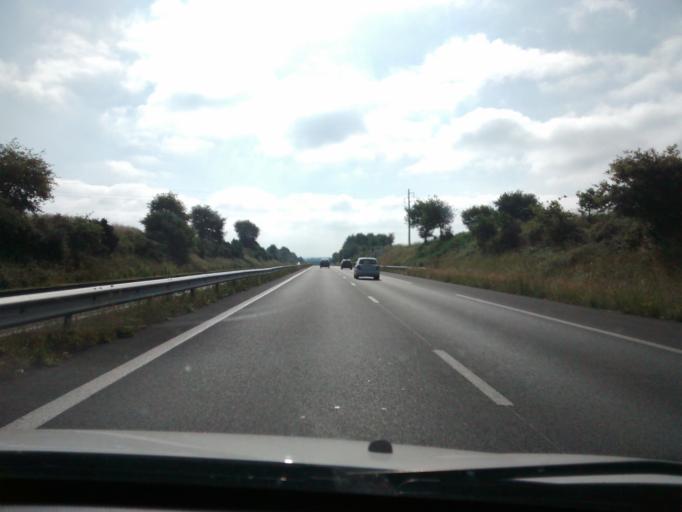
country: FR
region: Brittany
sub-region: Departement d'Ille-et-Vilaine
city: Etrelles
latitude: 48.0719
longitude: -1.2262
